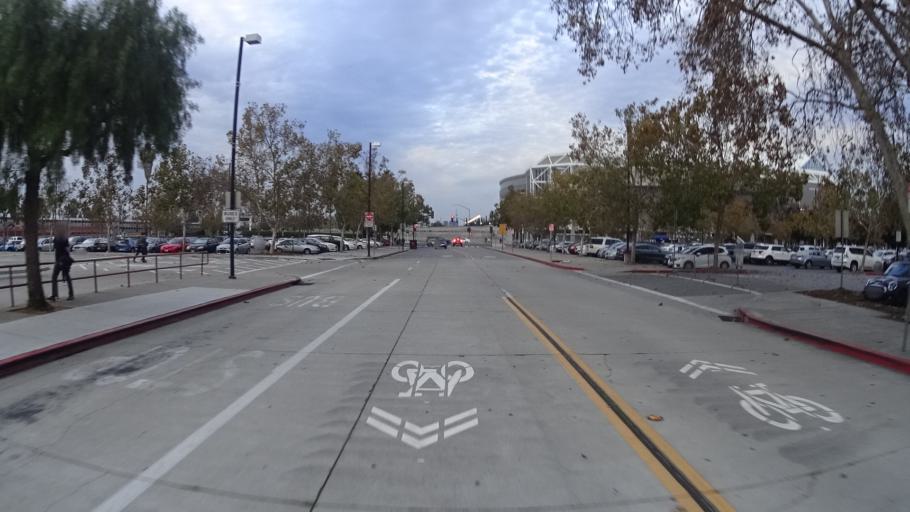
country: US
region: California
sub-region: Santa Clara County
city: San Jose
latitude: 37.3308
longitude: -121.9022
